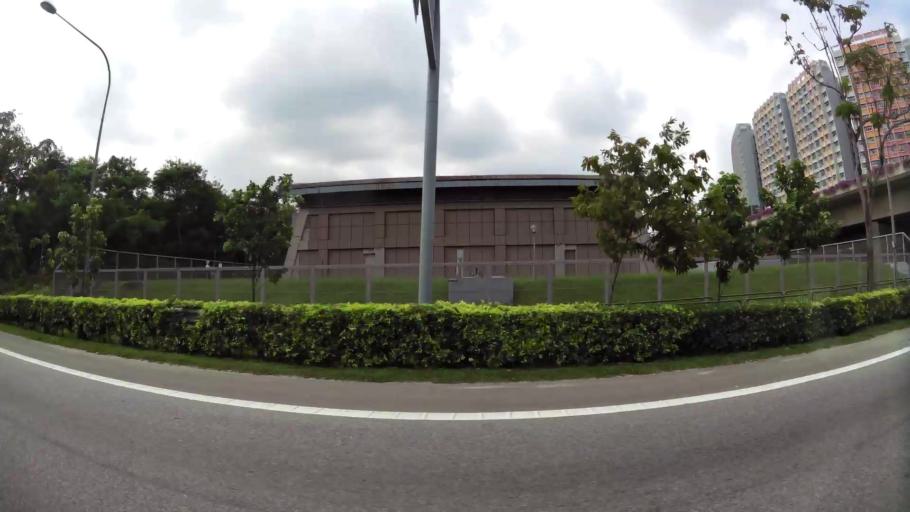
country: MY
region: Johor
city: Kampung Pasir Gudang Baru
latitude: 1.3886
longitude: 103.9118
